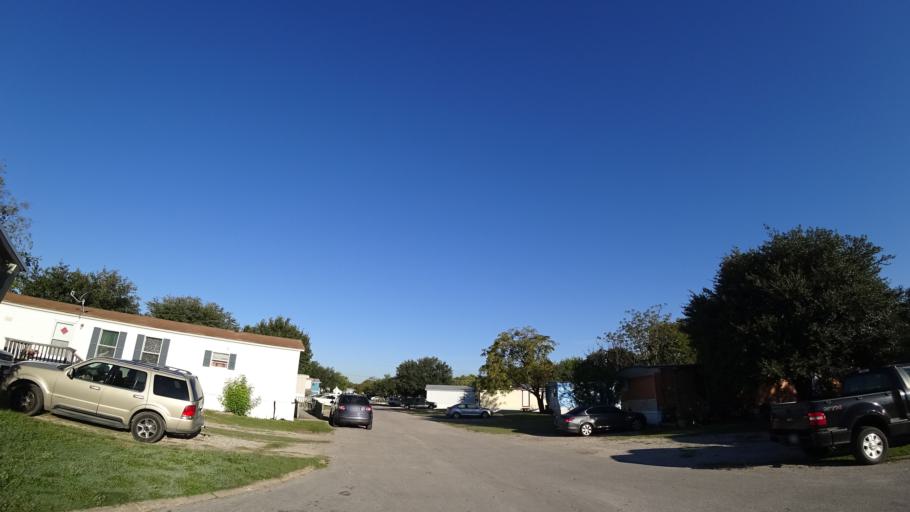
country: US
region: Texas
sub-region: Travis County
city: Austin
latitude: 30.2258
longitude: -97.6929
